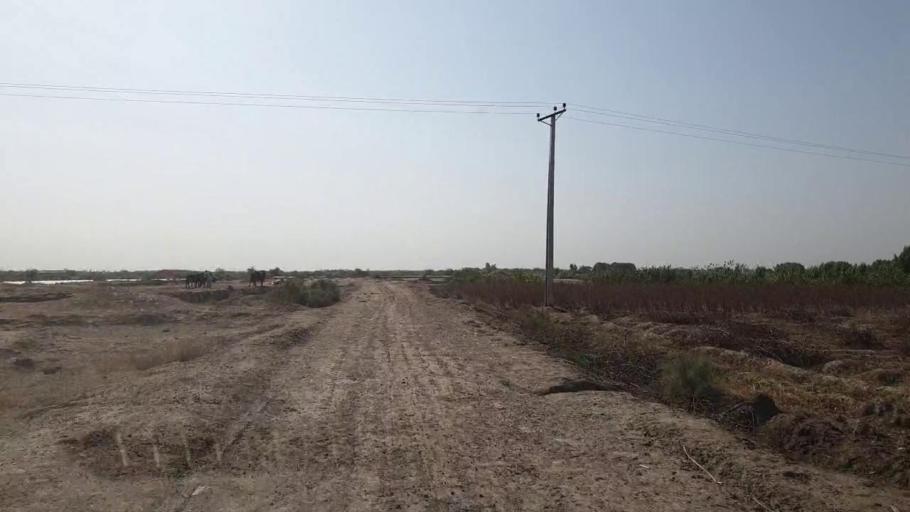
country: PK
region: Sindh
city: Kadhan
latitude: 24.6131
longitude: 69.0692
